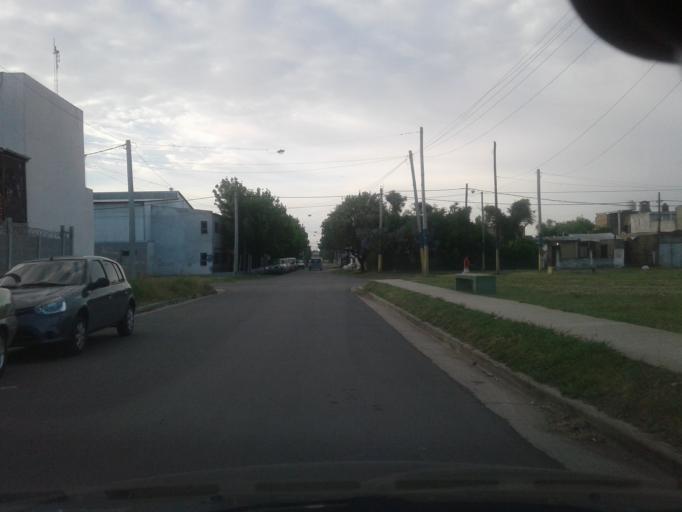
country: AR
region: Santa Fe
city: Granadero Baigorria
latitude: -32.8847
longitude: -60.7257
